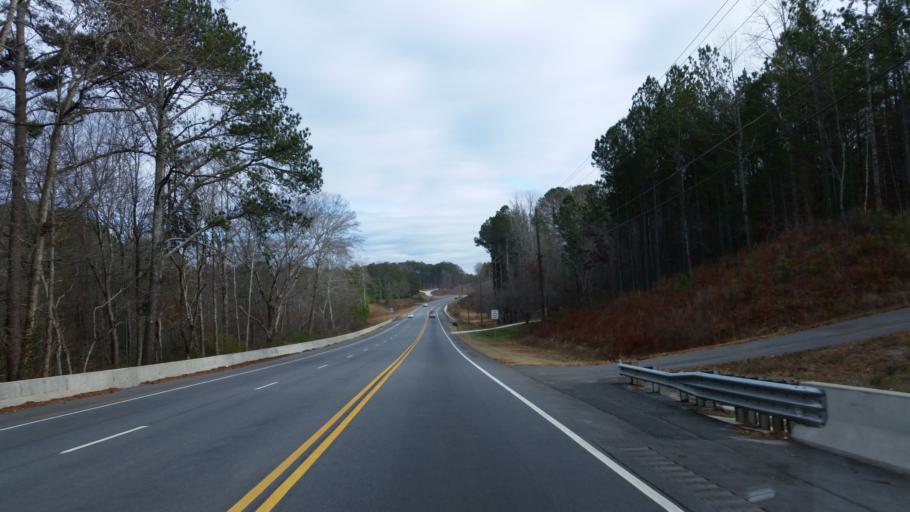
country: US
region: Georgia
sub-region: Bartow County
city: Emerson
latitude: 34.2220
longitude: -84.7036
